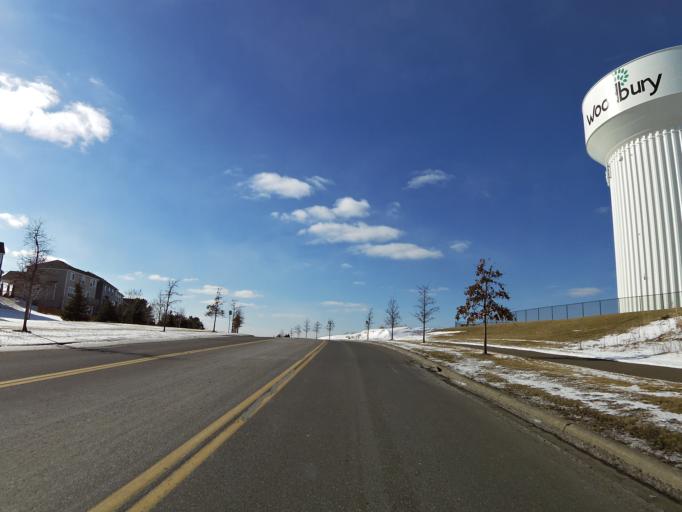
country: US
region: Minnesota
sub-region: Washington County
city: Afton
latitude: 44.9019
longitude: -92.8647
